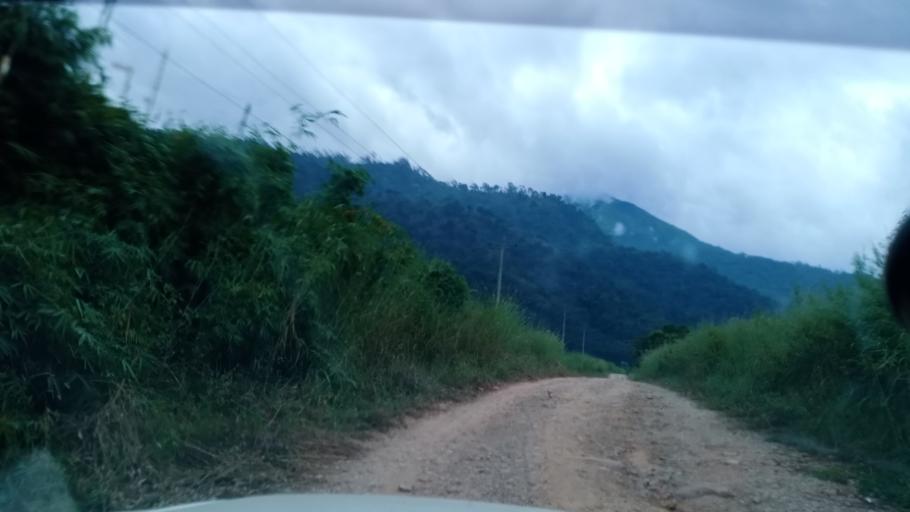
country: TH
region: Changwat Bueng Kan
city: Pak Khat
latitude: 18.7229
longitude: 103.2359
